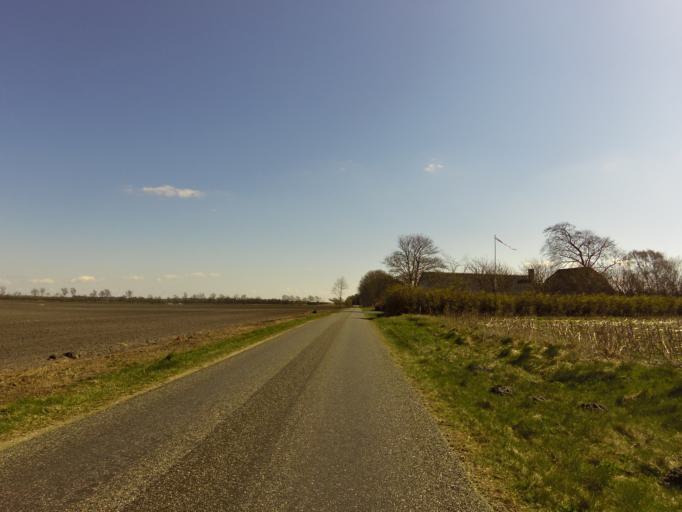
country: DK
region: South Denmark
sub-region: Esbjerg Kommune
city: Ribe
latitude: 55.3418
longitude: 8.8592
